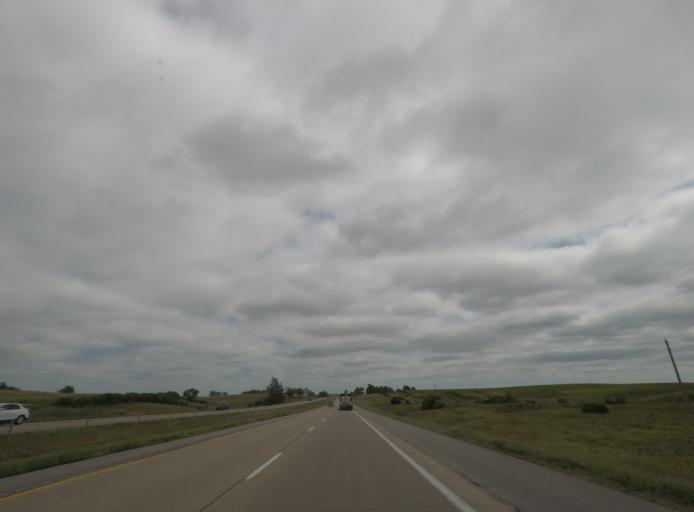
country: US
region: Iowa
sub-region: Poweshiek County
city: Brooklyn
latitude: 41.6961
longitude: -92.4082
